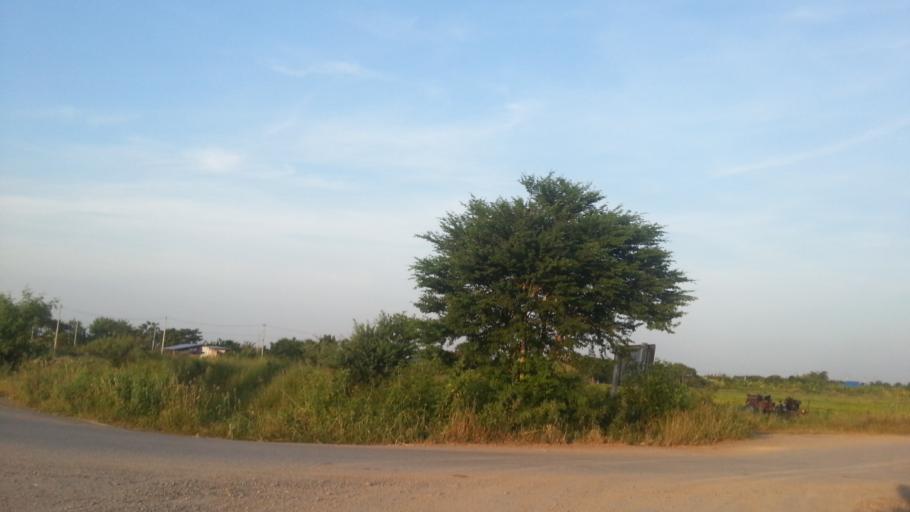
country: TH
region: Pathum Thani
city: Ban Lam Luk Ka
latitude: 14.0369
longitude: 100.8567
